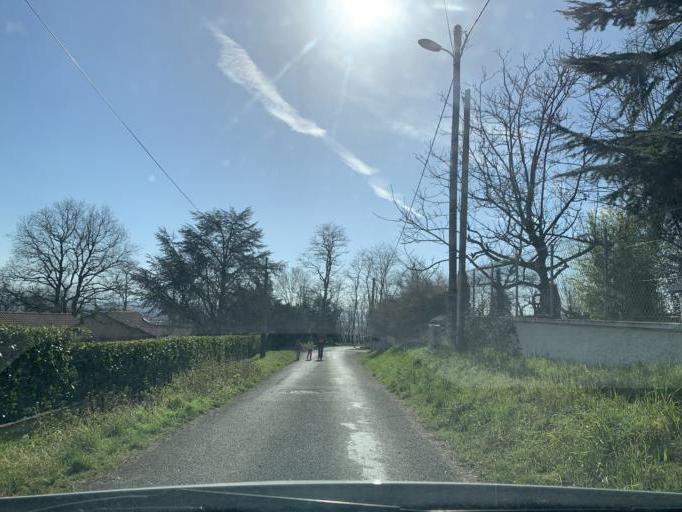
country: FR
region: Rhone-Alpes
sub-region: Departement du Rhone
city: Rillieux-la-Pape
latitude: 45.8122
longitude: 4.9228
